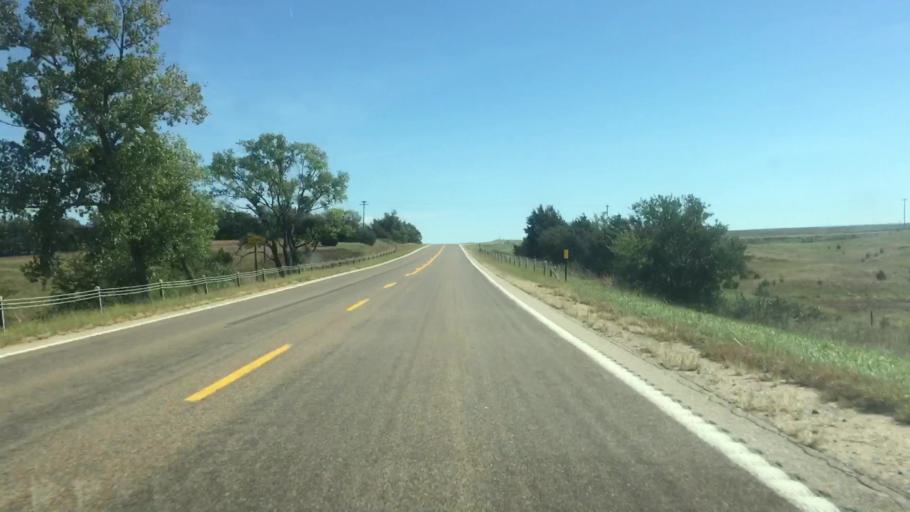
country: US
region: Nebraska
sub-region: Thayer County
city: Hebron
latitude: 40.1472
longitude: -97.5415
